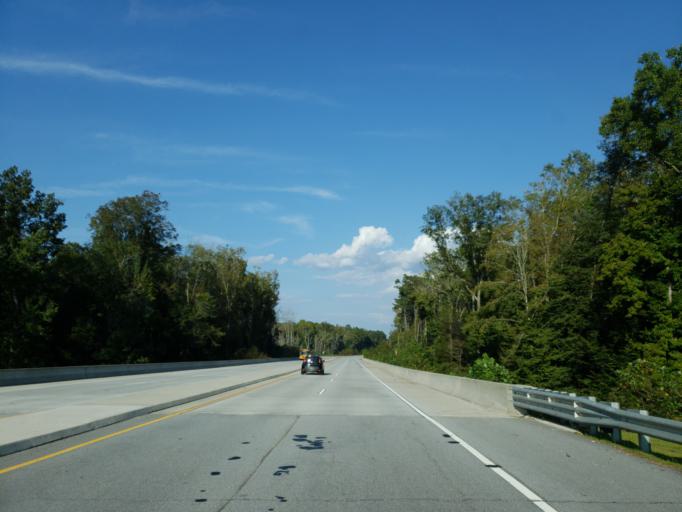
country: US
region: Georgia
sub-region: Paulding County
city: Hiram
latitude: 33.8579
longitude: -84.7553
